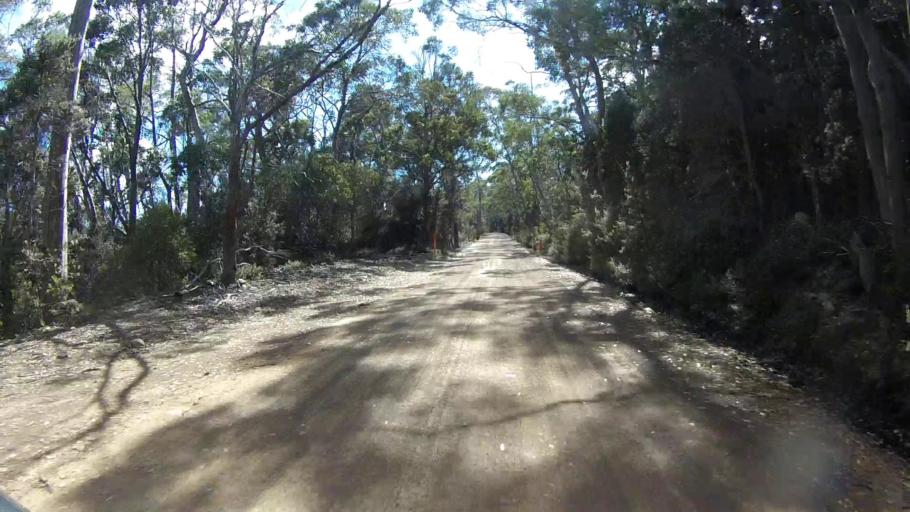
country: AU
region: Tasmania
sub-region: Derwent Valley
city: New Norfolk
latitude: -42.6867
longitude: 146.6036
